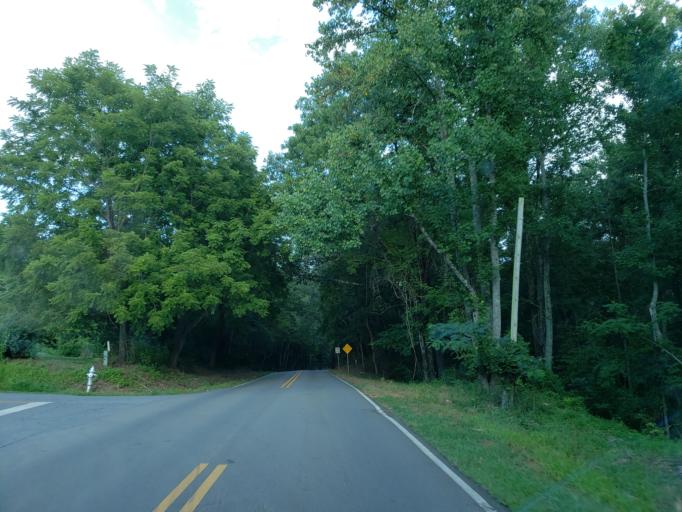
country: US
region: Georgia
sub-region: Cherokee County
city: Ball Ground
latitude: 34.3358
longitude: -84.4425
